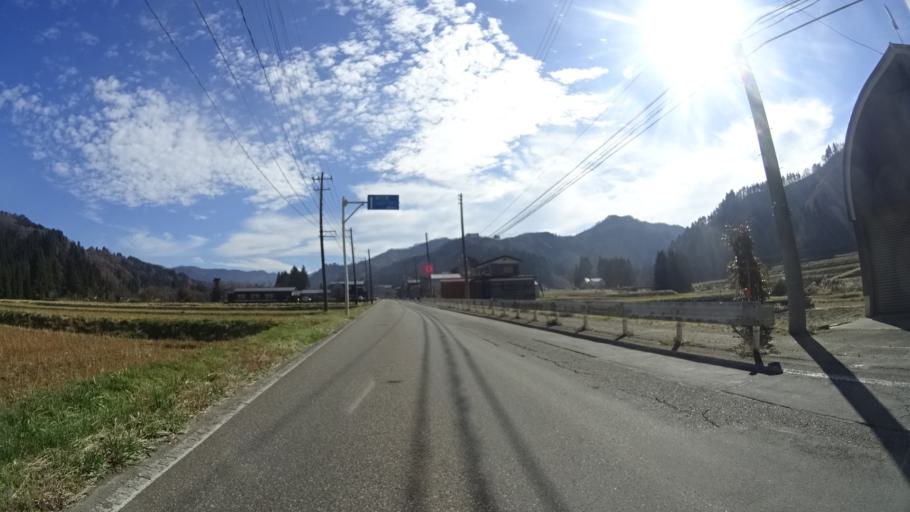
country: JP
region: Niigata
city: Muikamachi
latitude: 37.2179
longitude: 139.0352
